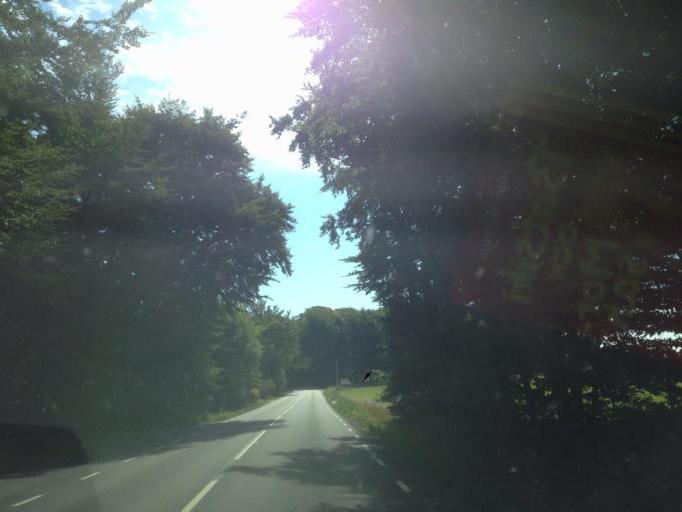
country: SE
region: Skane
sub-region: Tomelilla Kommun
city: Tomelilla
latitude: 55.6346
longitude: 14.0889
